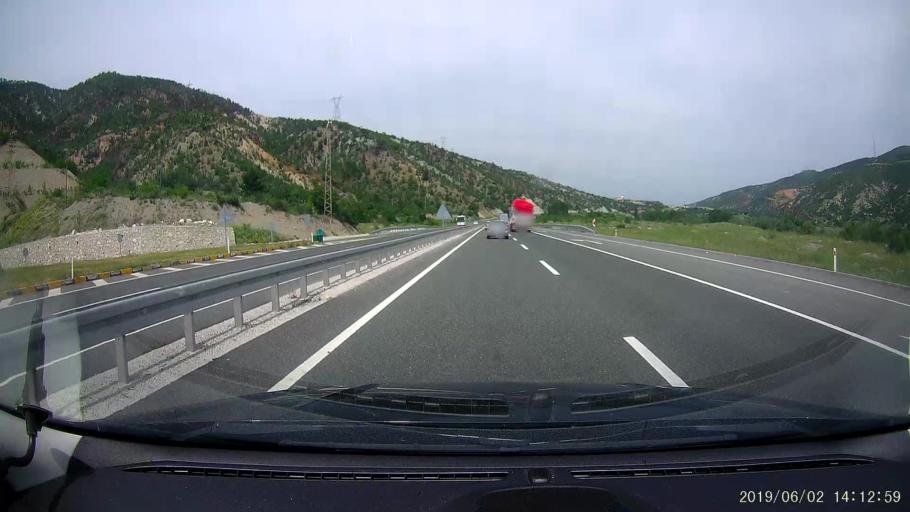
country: TR
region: Cankiri
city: Yaprakli
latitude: 40.9214
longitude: 33.8194
